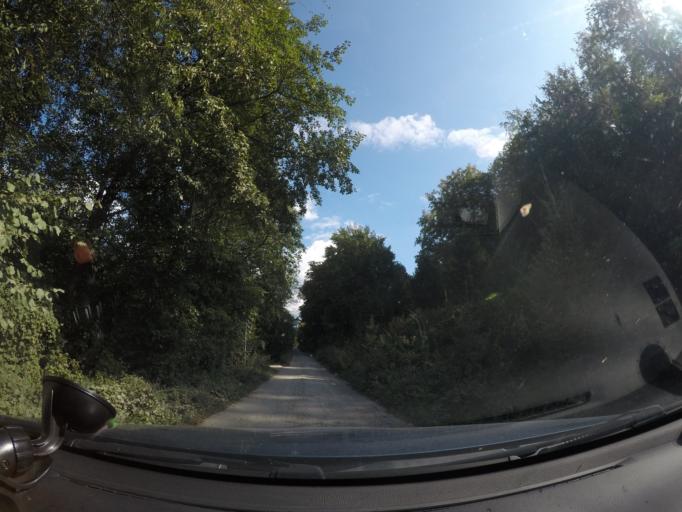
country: SK
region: Trenciansky
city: Nova Dubnica
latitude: 48.9022
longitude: 18.1231
